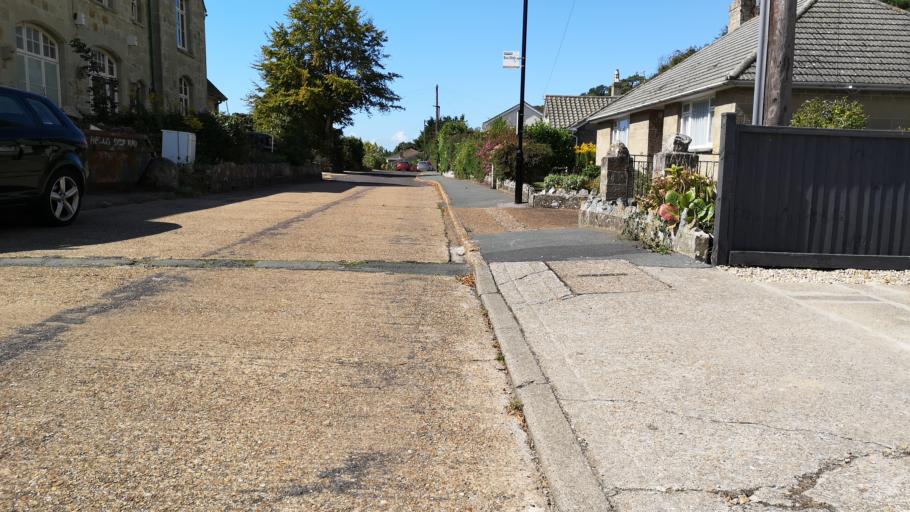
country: GB
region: England
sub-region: Isle of Wight
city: Ventnor
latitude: 50.5925
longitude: -1.2189
